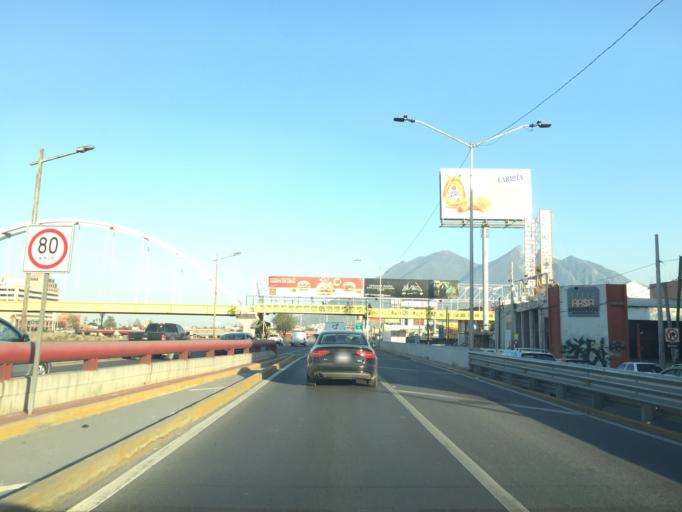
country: MX
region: Nuevo Leon
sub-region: Monterrey
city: Monterrey
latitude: 25.6629
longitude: -100.3174
